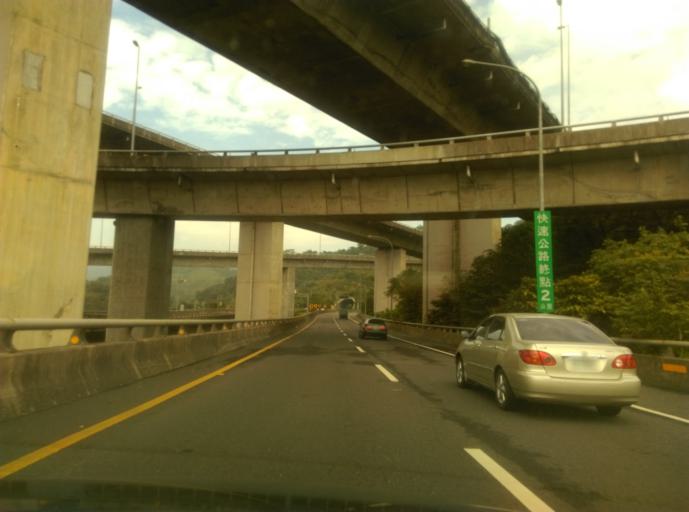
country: TW
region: Taiwan
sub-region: Keelung
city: Keelung
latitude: 25.1264
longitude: 121.6980
